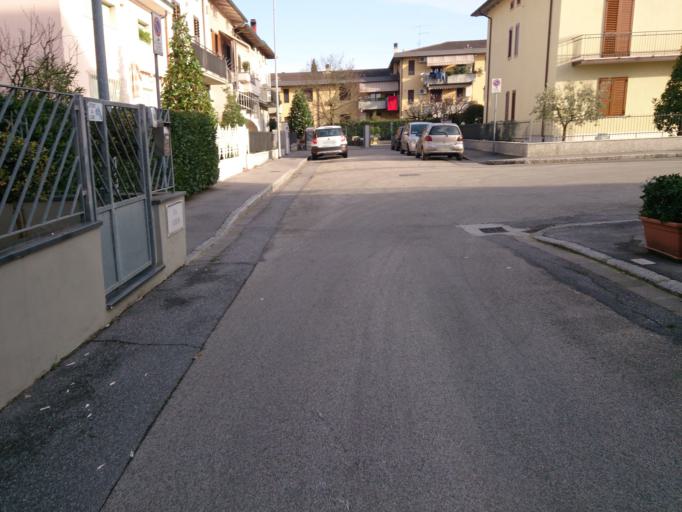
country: IT
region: Tuscany
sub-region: Provincia di Prato
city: Fornacelle
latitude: 43.8913
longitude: 11.0486
